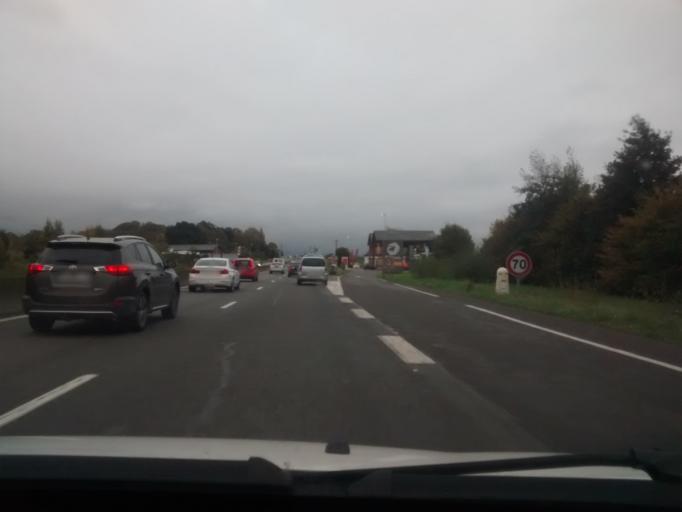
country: FR
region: Brittany
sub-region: Departement d'Ille-et-Vilaine
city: Saint-Jouan-des-Guerets
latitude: 48.6145
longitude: -1.9836
